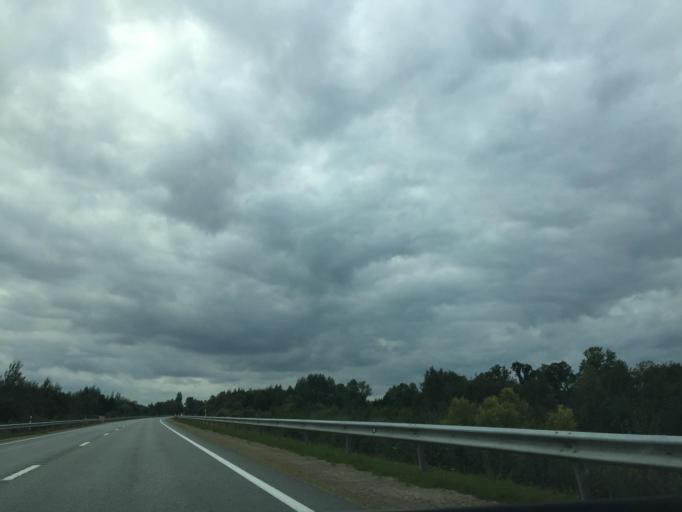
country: LV
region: Aizkraukles Rajons
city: Aizkraukle
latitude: 56.7054
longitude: 25.2471
